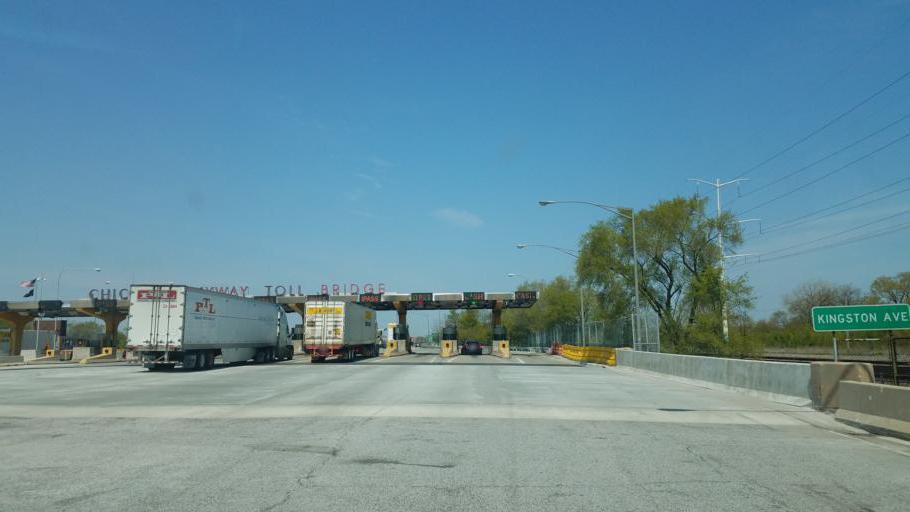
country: US
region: Indiana
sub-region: Lake County
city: Whiting
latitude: 41.7340
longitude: -87.5636
